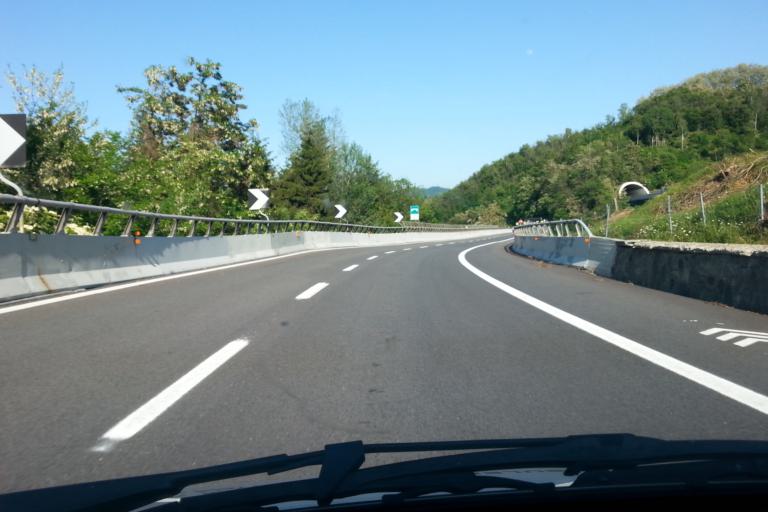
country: IT
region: Liguria
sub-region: Provincia di Savona
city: Valzemola
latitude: 44.3582
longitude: 8.1706
